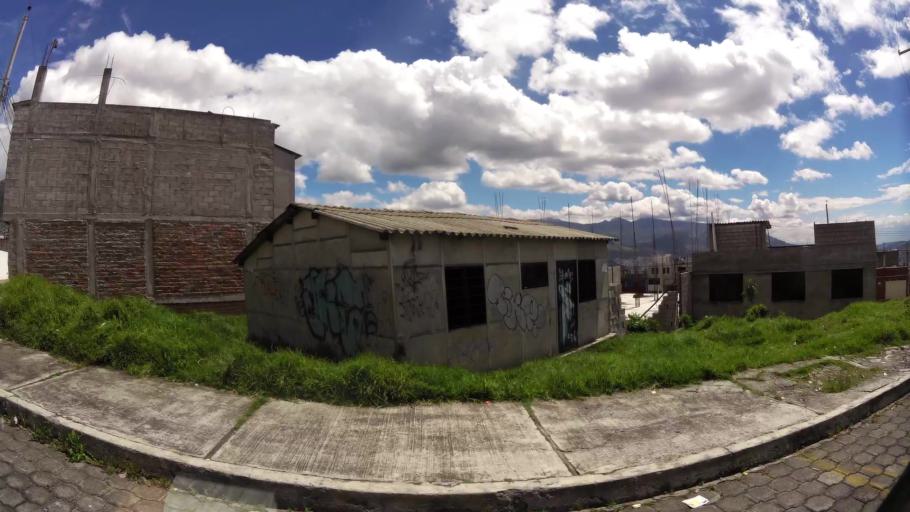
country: EC
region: Pichincha
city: Quito
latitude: -0.3327
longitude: -78.5629
